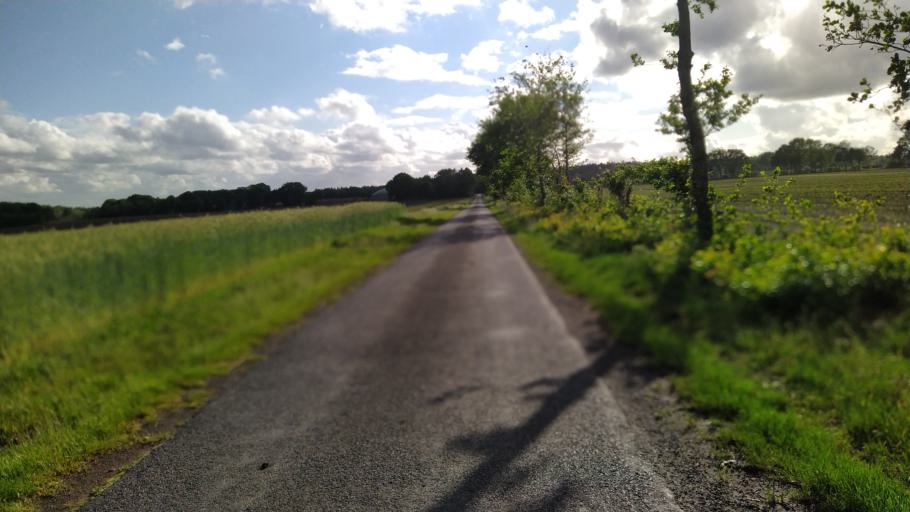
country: DE
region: Lower Saxony
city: Farven
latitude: 53.4431
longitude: 9.3114
